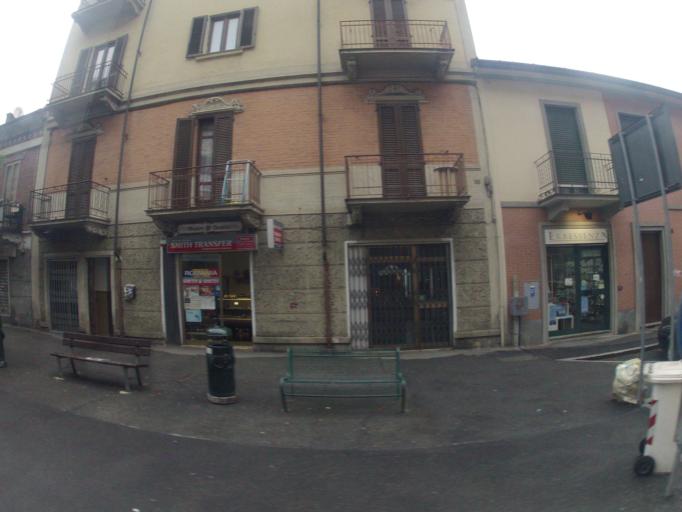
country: IT
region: Piedmont
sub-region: Provincia di Torino
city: Nichelino
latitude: 45.0153
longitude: 7.6629
